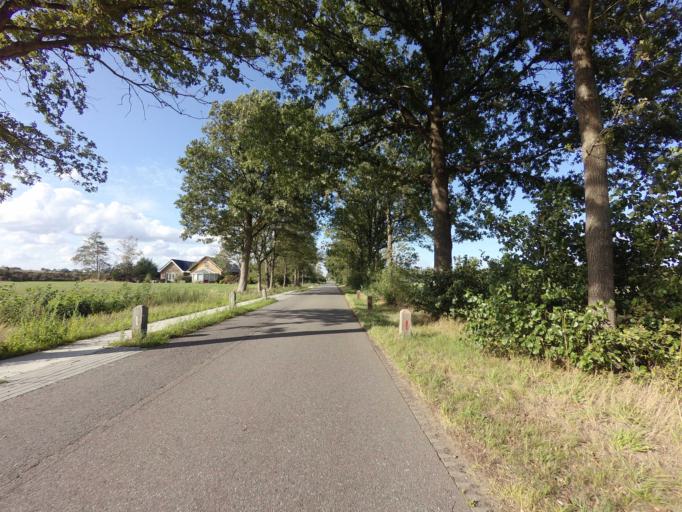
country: NL
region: Friesland
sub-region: Gemeente Heerenveen
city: Jubbega
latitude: 53.0117
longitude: 6.2325
